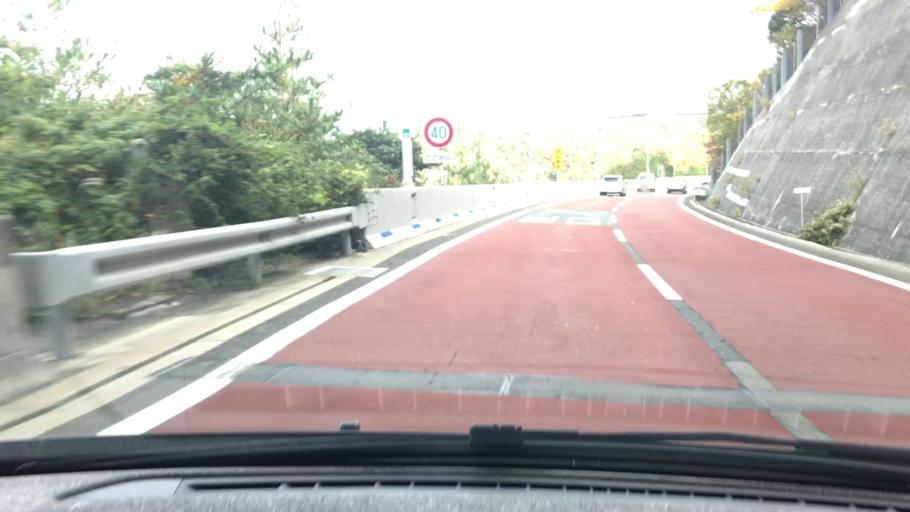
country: JP
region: Hyogo
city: Sandacho
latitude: 34.8290
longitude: 135.2570
